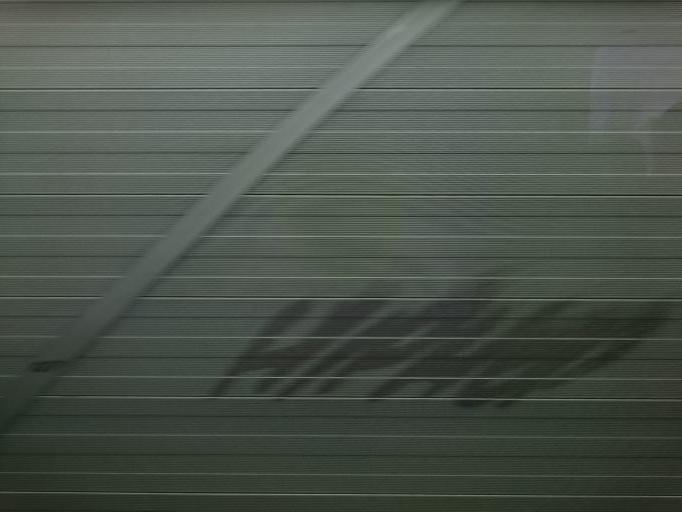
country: DE
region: Bavaria
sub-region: Upper Bavaria
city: Haar
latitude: 48.1223
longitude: 11.6799
